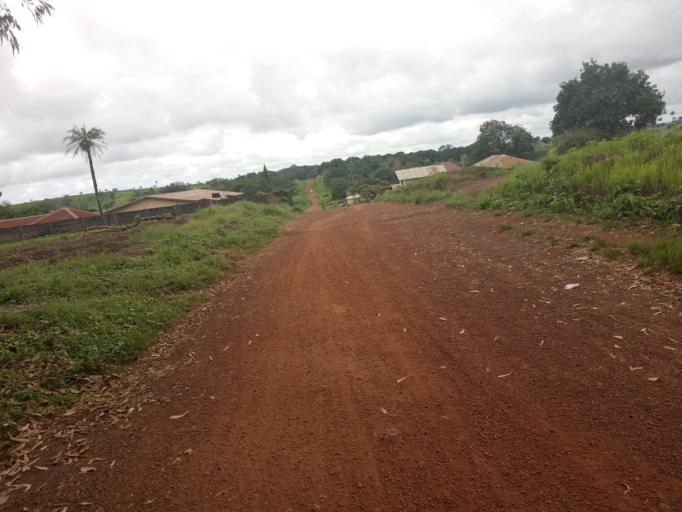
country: SL
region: Northern Province
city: Kamakwie
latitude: 9.5017
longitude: -12.2518
